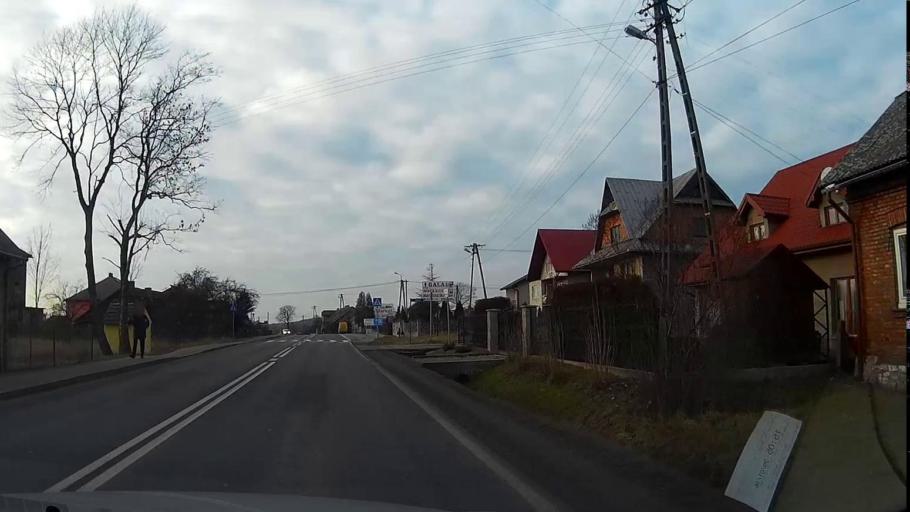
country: PL
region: Lesser Poland Voivodeship
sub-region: Powiat chrzanowski
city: Brodla
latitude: 50.0434
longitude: 19.5877
